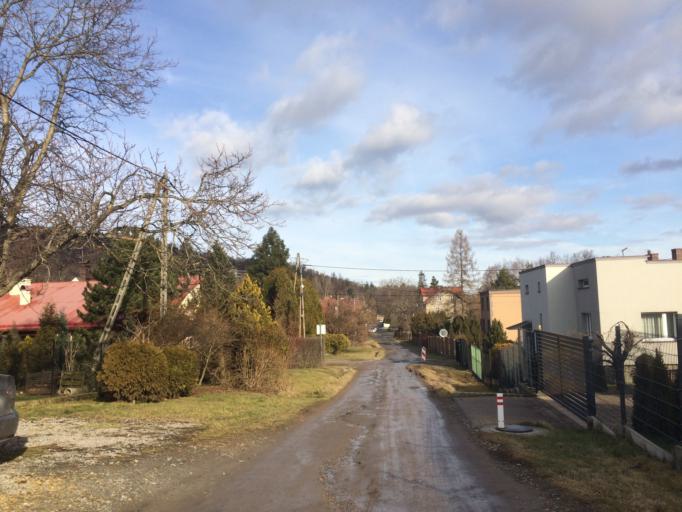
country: PL
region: Silesian Voivodeship
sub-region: Powiat bielski
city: Bystra
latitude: 49.7590
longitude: 19.0689
